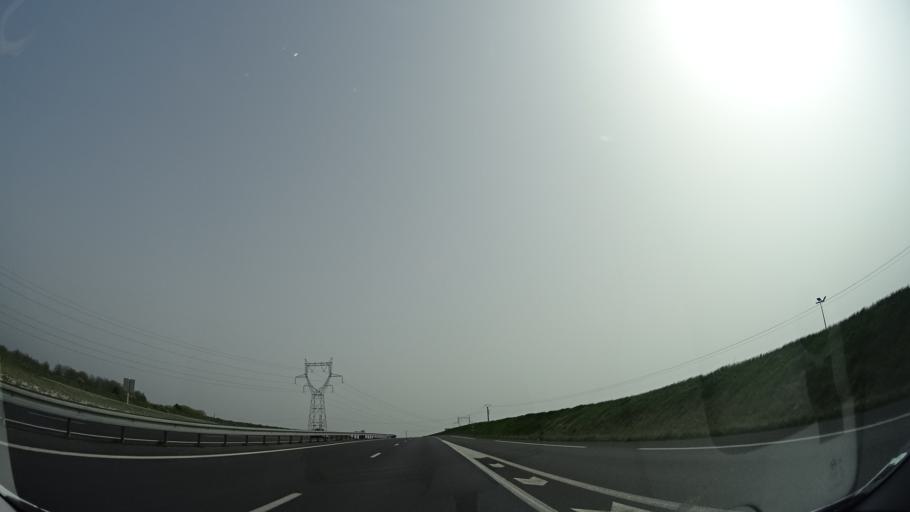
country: FR
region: Pays de la Loire
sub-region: Departement de Maine-et-Loire
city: Doue-la-Fontaine
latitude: 47.2002
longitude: -0.2177
